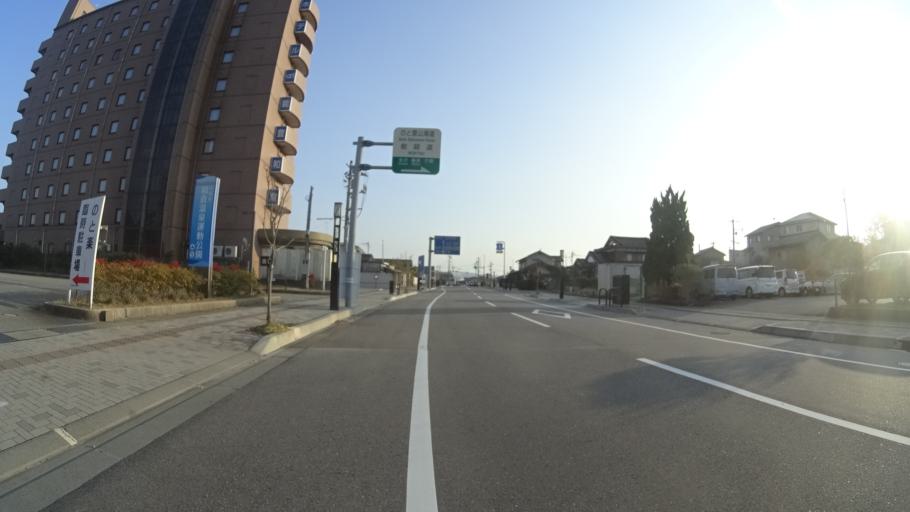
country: JP
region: Ishikawa
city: Nanao
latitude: 37.0846
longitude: 136.9259
